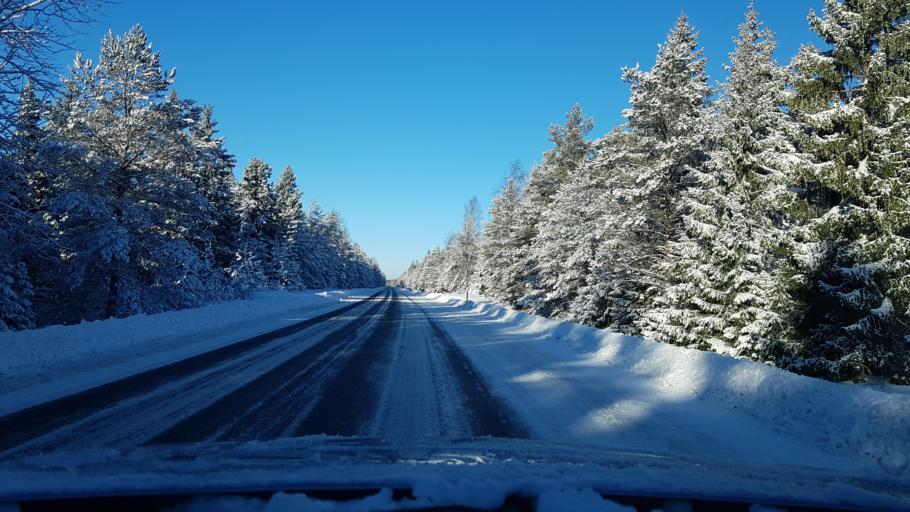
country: EE
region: Hiiumaa
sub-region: Kaerdla linn
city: Kardla
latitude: 58.9820
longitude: 22.8071
